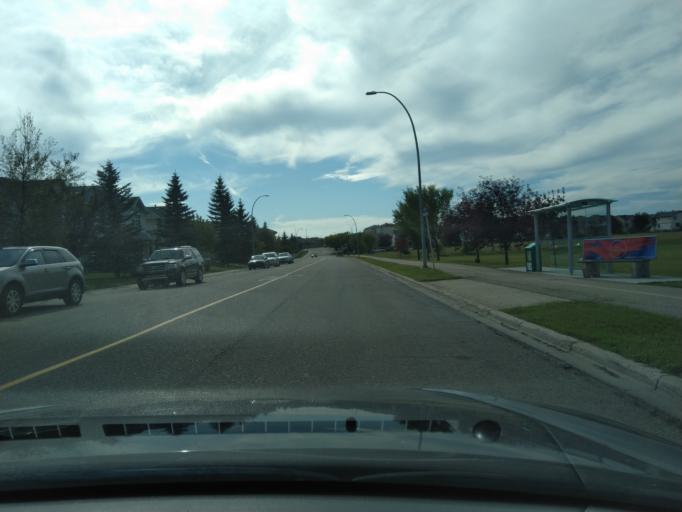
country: CA
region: Alberta
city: Calgary
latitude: 51.1466
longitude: -114.0688
